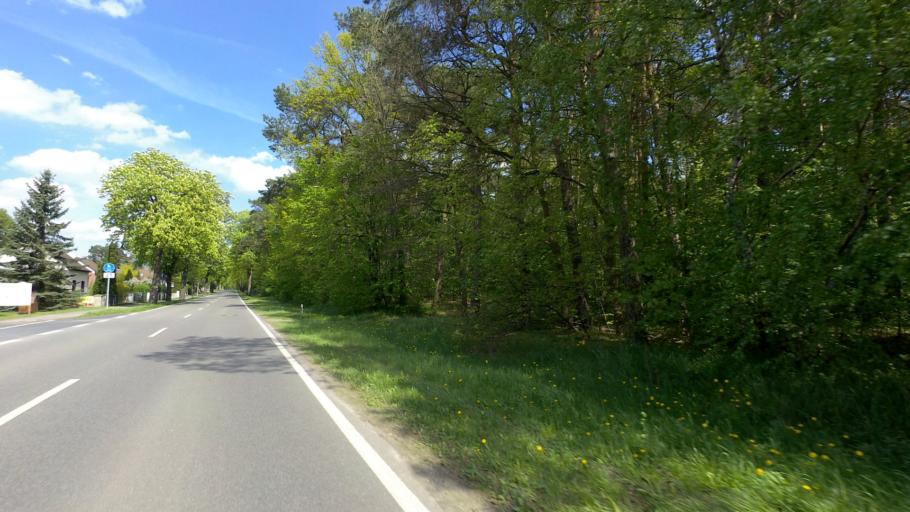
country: DE
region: Brandenburg
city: Wandlitz
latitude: 52.8008
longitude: 13.4836
